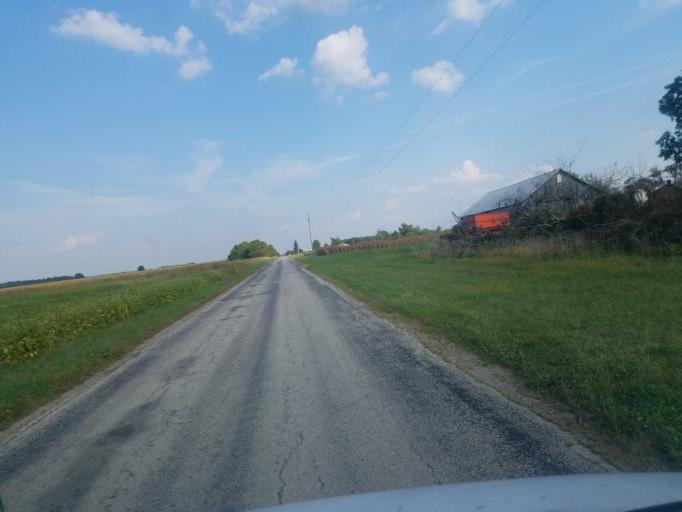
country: US
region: Ohio
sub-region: Hardin County
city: Forest
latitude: 40.9053
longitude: -83.5251
